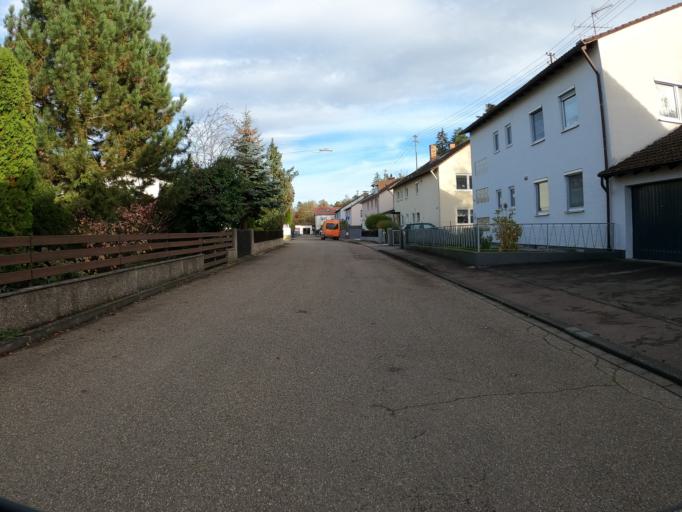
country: DE
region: Bavaria
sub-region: Swabia
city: Nersingen
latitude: 48.4140
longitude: 10.1495
